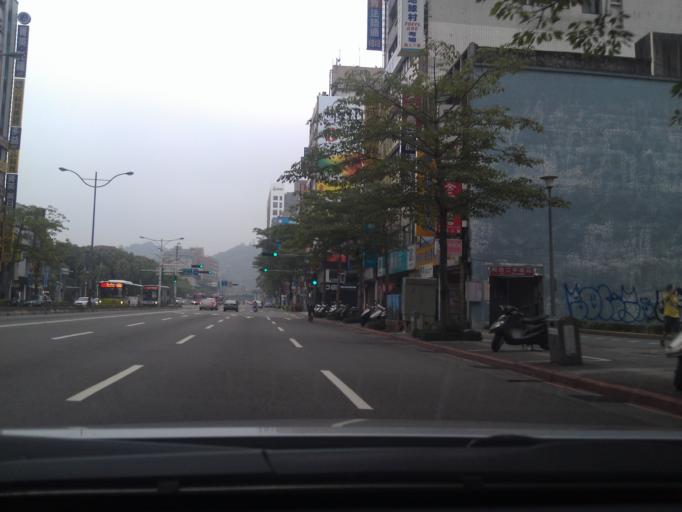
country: TW
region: Taipei
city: Taipei
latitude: 25.0172
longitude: 121.5316
